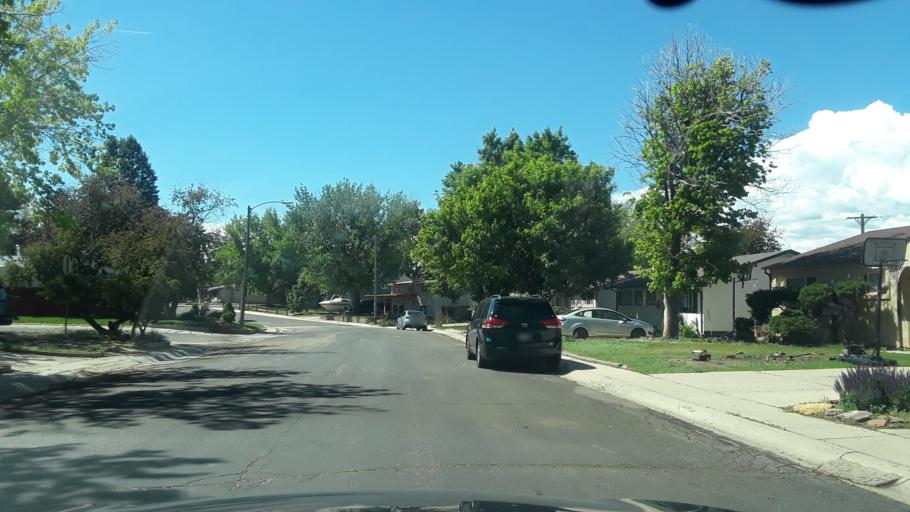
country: US
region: Colorado
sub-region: El Paso County
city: Colorado Springs
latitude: 38.8953
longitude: -104.8169
